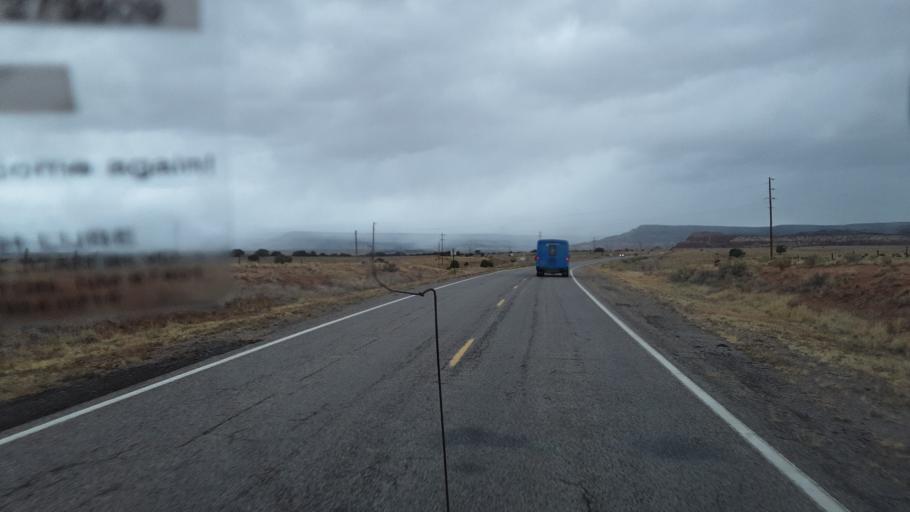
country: US
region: New Mexico
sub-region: Rio Arriba County
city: Santa Teresa
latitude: 36.2641
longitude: -106.4209
